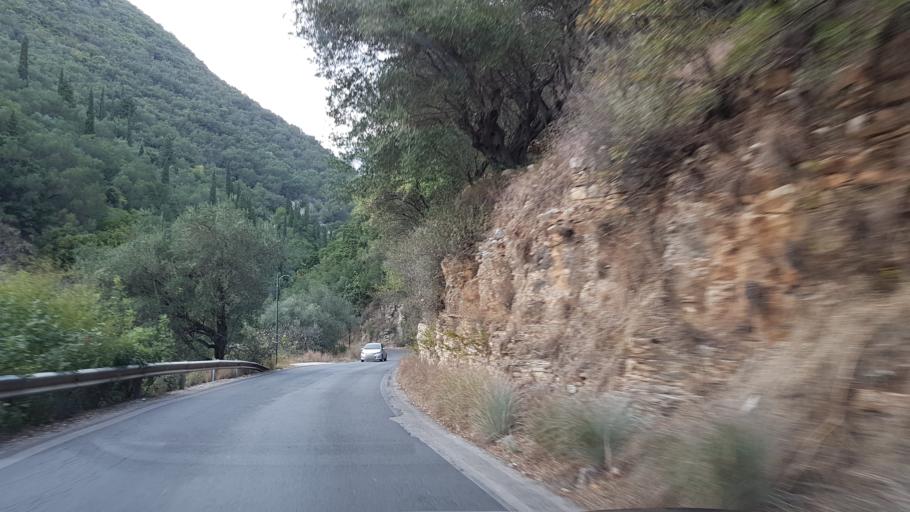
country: GR
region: Ionian Islands
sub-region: Nomos Kerkyras
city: Kontokali
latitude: 39.7350
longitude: 19.9197
